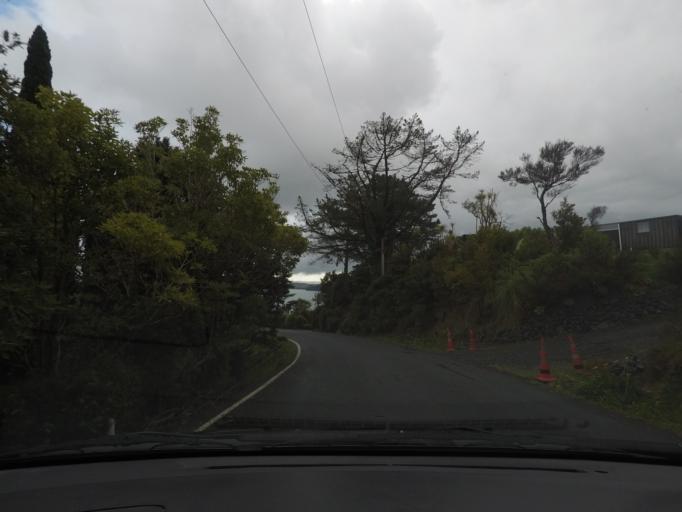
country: NZ
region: Auckland
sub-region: Auckland
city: Warkworth
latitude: -36.4739
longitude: 174.7338
